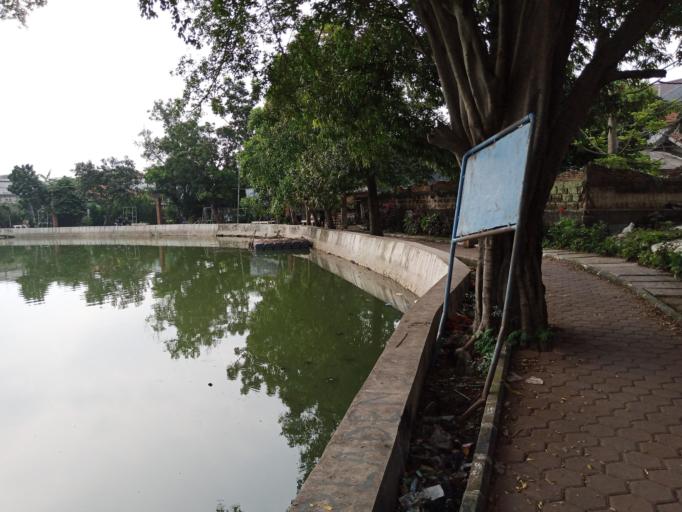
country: ID
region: West Java
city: Depok
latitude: -6.3872
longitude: 106.8200
